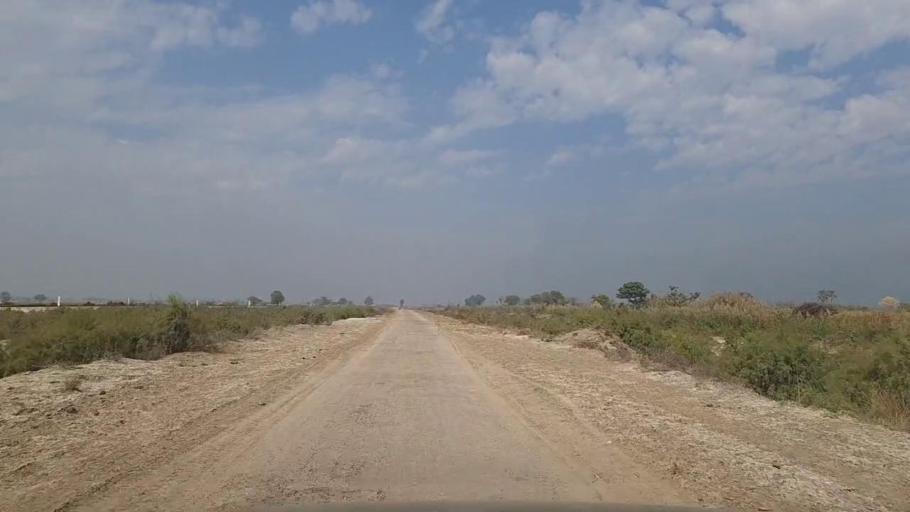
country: PK
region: Sindh
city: Daur
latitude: 26.3924
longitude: 68.3496
